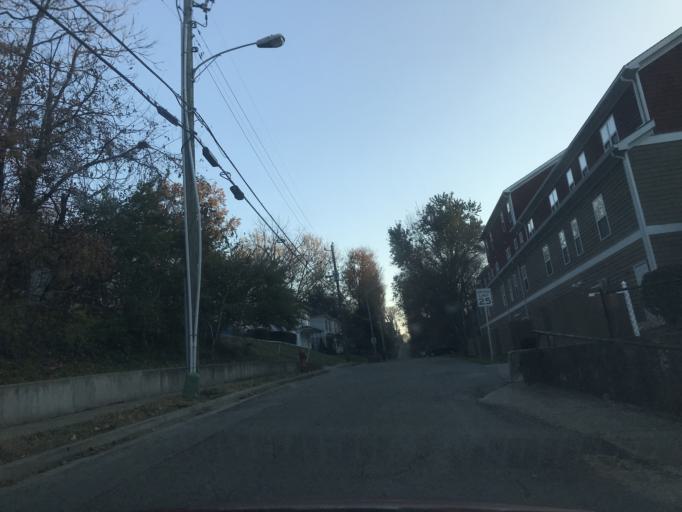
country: US
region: Indiana
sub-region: Clark County
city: Jeffersonville
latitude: 38.2575
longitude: -85.7036
